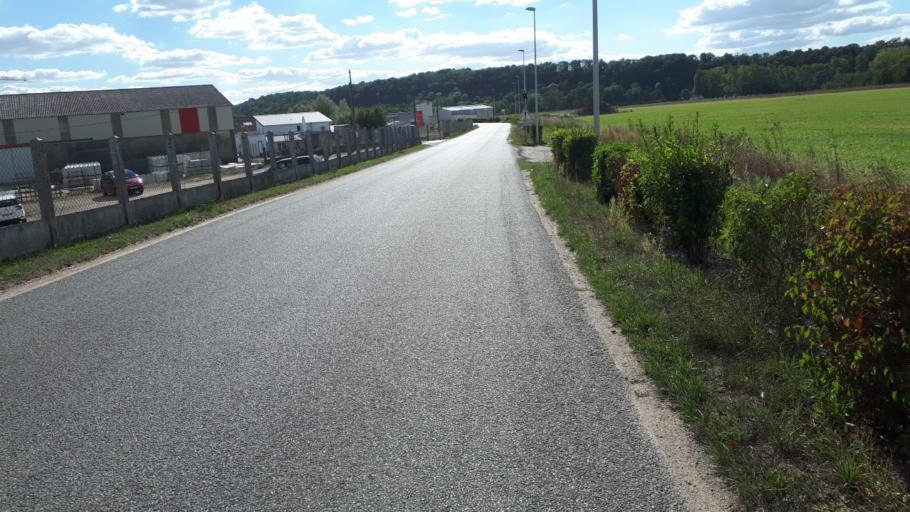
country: FR
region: Centre
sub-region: Departement du Loir-et-Cher
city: Villiers-sur-Loir
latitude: 47.7972
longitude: 0.9638
